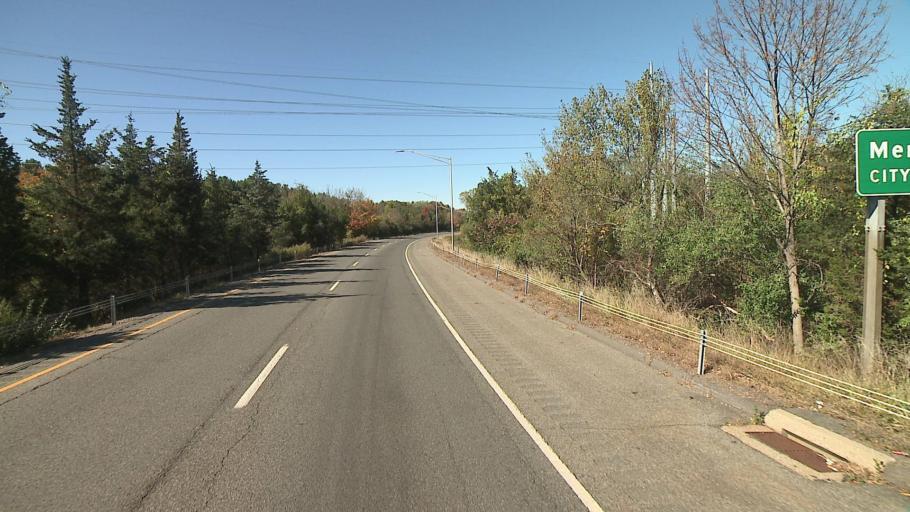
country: US
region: Connecticut
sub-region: New Haven County
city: Meriden
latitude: 41.5287
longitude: -72.7474
